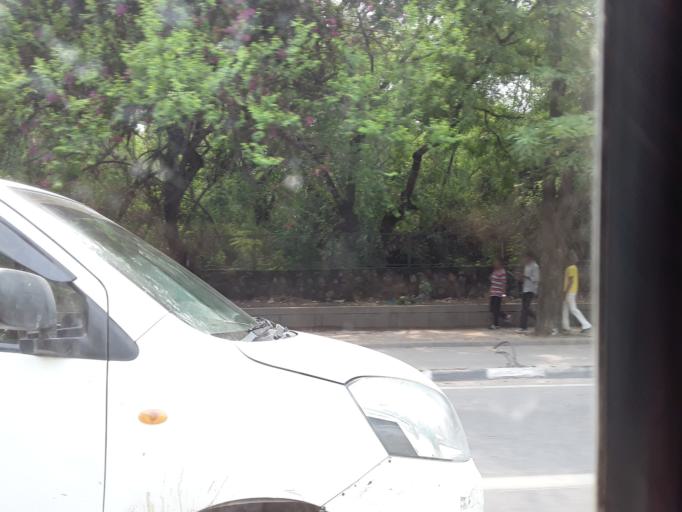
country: IN
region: NCT
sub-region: New Delhi
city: New Delhi
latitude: 28.5512
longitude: 77.2283
